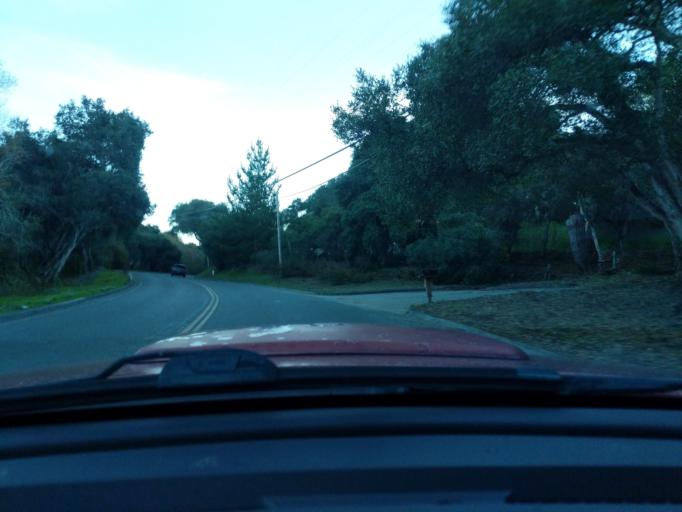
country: US
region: California
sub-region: San Benito County
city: Aromas
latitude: 36.8536
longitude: -121.6813
